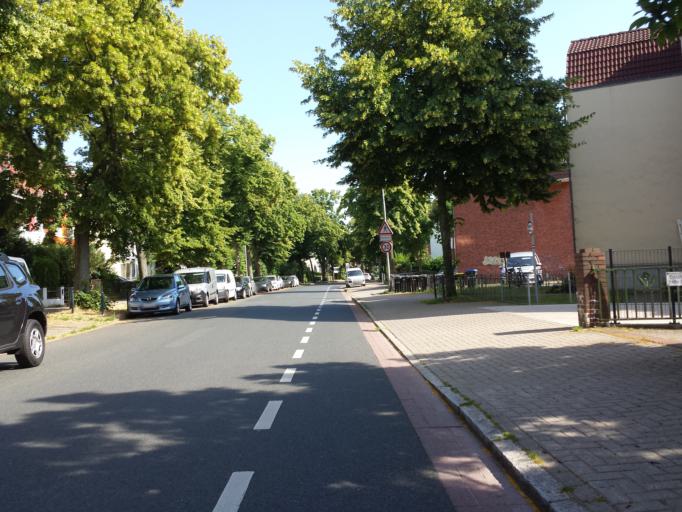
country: DE
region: Lower Saxony
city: Stuhr
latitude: 53.0930
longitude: 8.7498
